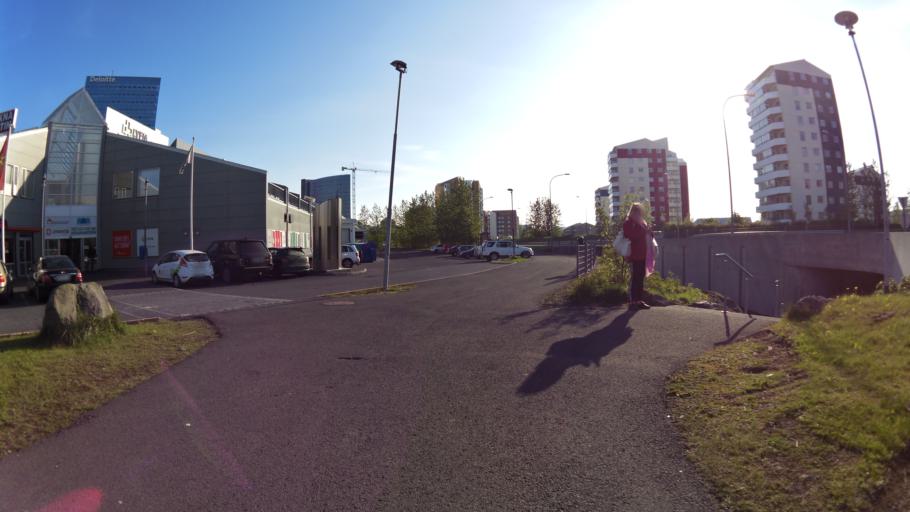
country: IS
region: Capital Region
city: Reykjavik
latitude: 64.1043
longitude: -21.8779
